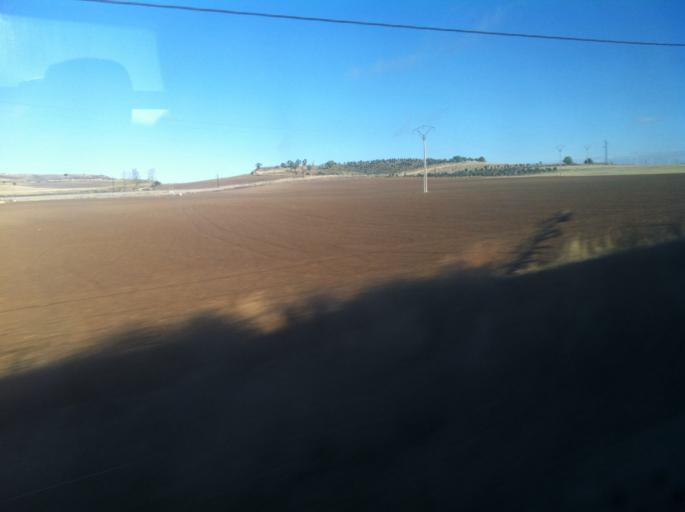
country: ES
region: Castille and Leon
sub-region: Provincia de Palencia
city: Palenzuela
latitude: 42.1264
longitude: -4.1424
